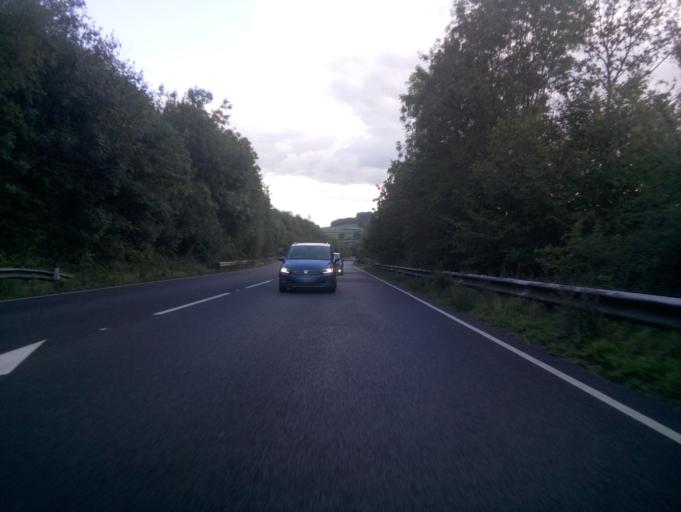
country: GB
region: England
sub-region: Somerset
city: Chard
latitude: 50.8962
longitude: -3.0525
